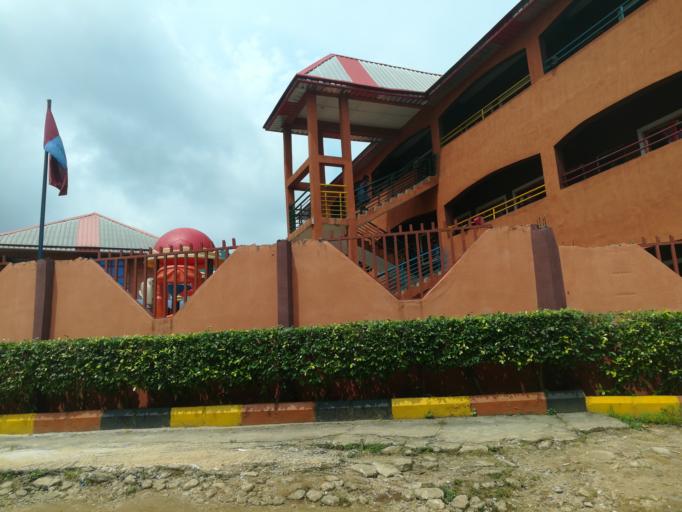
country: NG
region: Rivers
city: Port Harcourt
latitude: 4.8927
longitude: 6.9829
